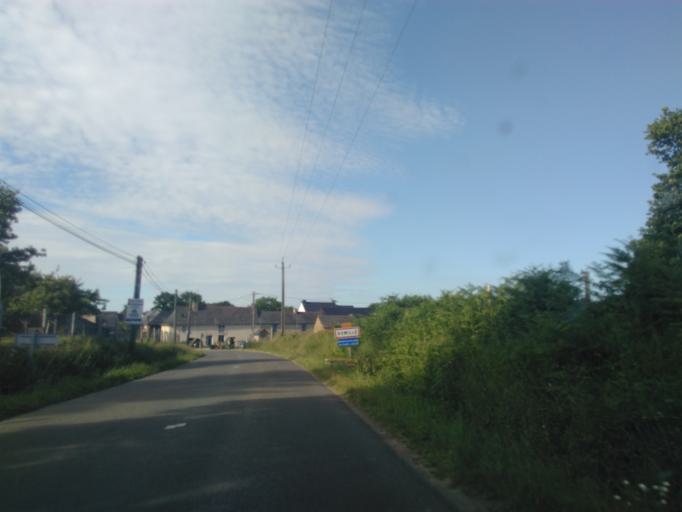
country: FR
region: Brittany
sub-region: Departement d'Ille-et-Vilaine
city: Romille
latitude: 48.2096
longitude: -1.8949
